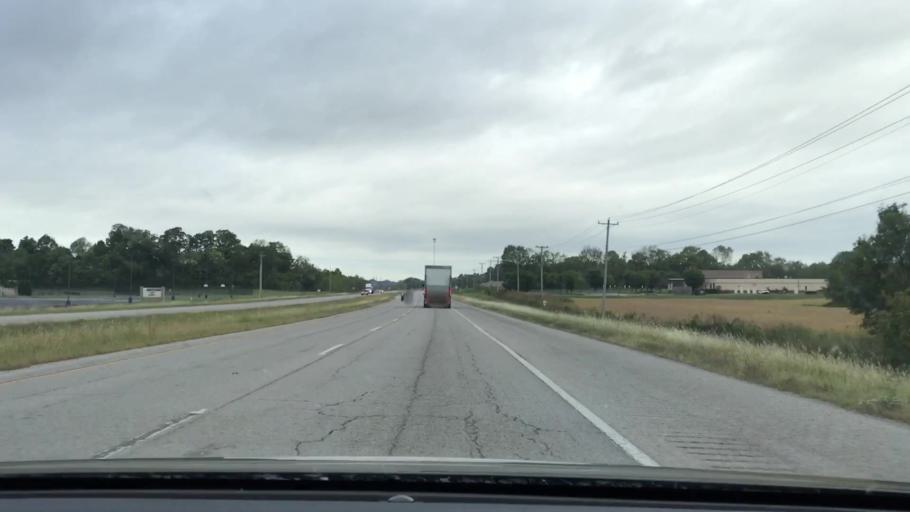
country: US
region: Kentucky
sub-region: Christian County
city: Hopkinsville
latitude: 36.8262
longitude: -87.5113
